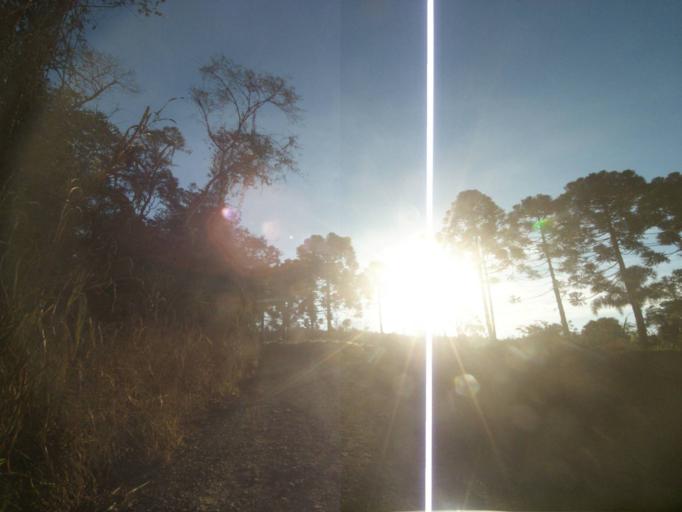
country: BR
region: Parana
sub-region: Telemaco Borba
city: Telemaco Borba
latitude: -24.4265
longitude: -50.5940
